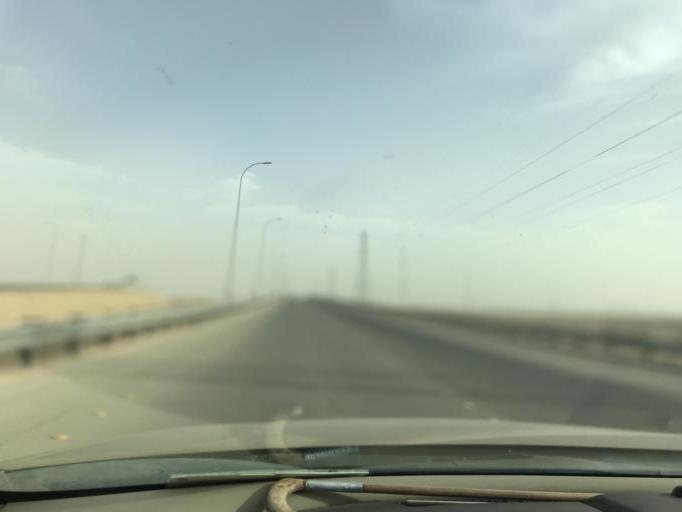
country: SA
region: Ar Riyad
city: Riyadh
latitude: 24.9065
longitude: 46.7033
